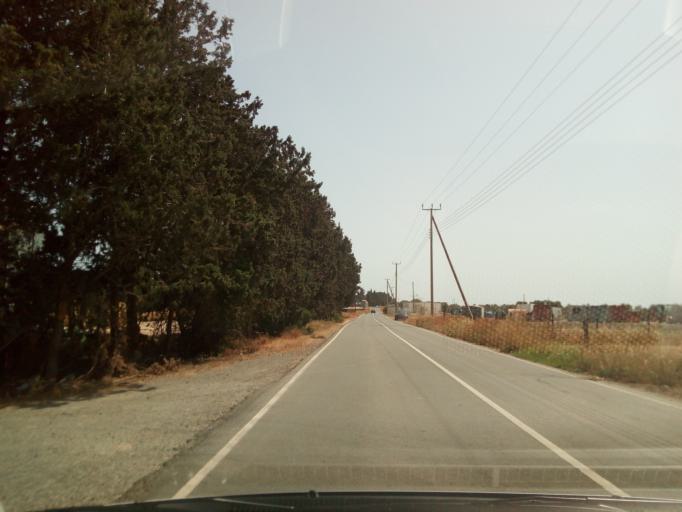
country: CY
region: Larnaka
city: Meneou
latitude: 34.8507
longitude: 33.5949
